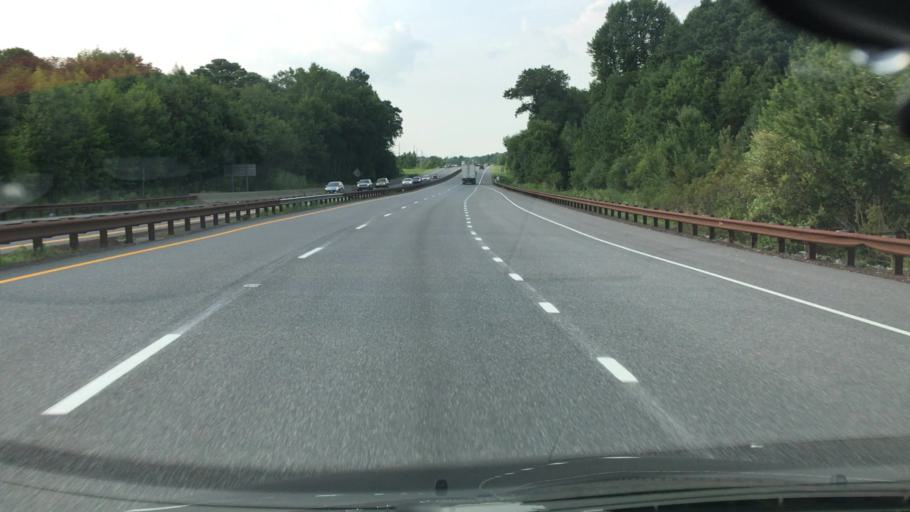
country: US
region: Delaware
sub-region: Sussex County
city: Selbyville
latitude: 38.4077
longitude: -75.2127
